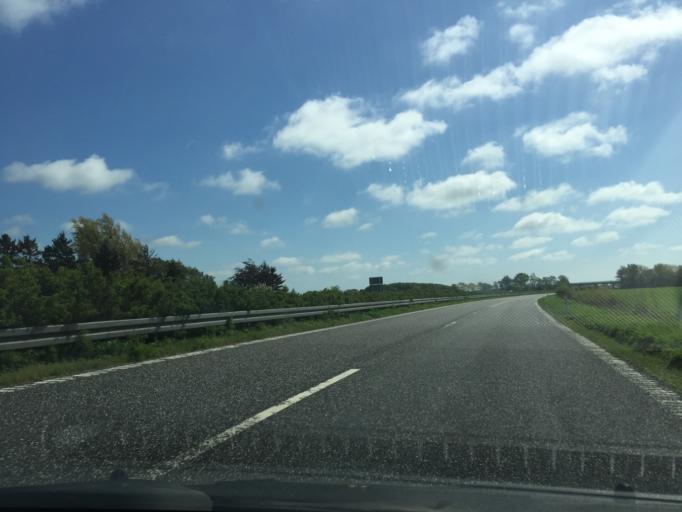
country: DK
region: Zealand
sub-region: Lolland Kommune
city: Maribo
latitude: 54.7563
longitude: 11.4617
